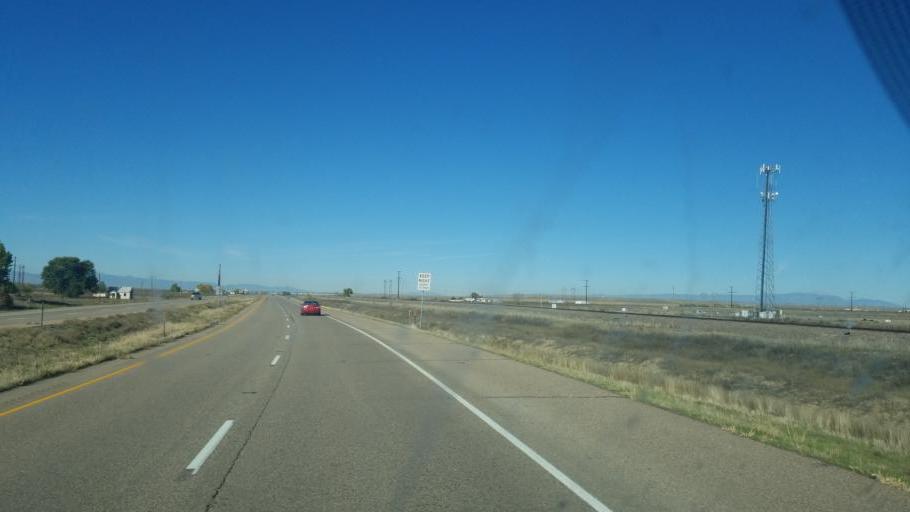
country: US
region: Colorado
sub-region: Pueblo County
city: Pueblo
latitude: 38.2674
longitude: -104.3765
